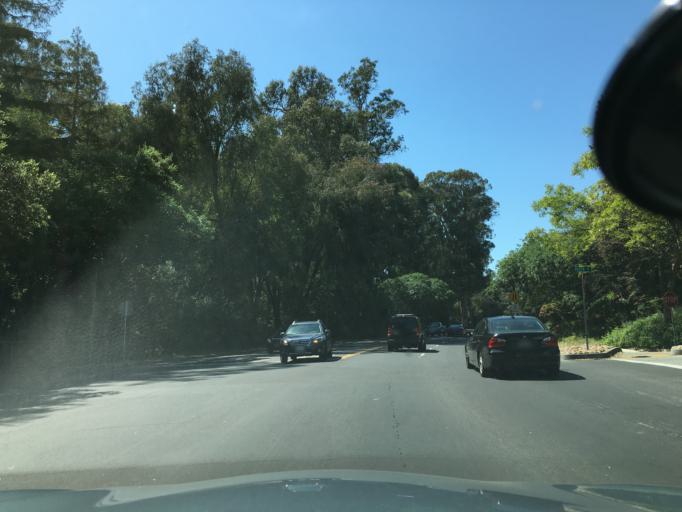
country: US
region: California
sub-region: San Mateo County
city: Belmont
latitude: 37.5170
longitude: -122.2787
